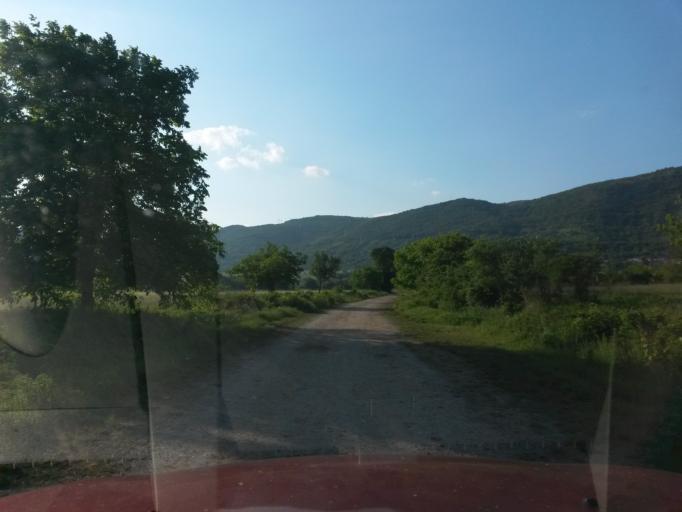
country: SK
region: Kosicky
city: Roznava
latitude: 48.5862
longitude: 20.6753
